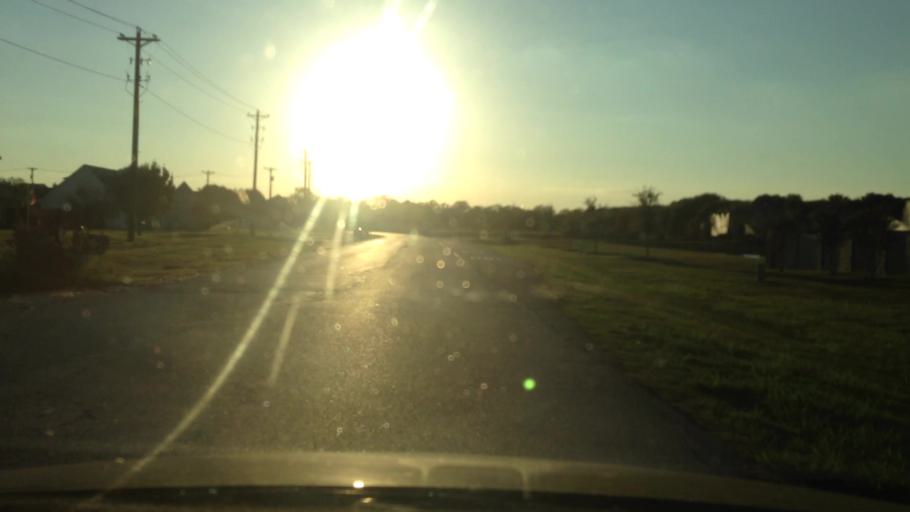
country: US
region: Texas
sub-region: Denton County
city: Little Elm
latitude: 33.1362
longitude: -96.9310
